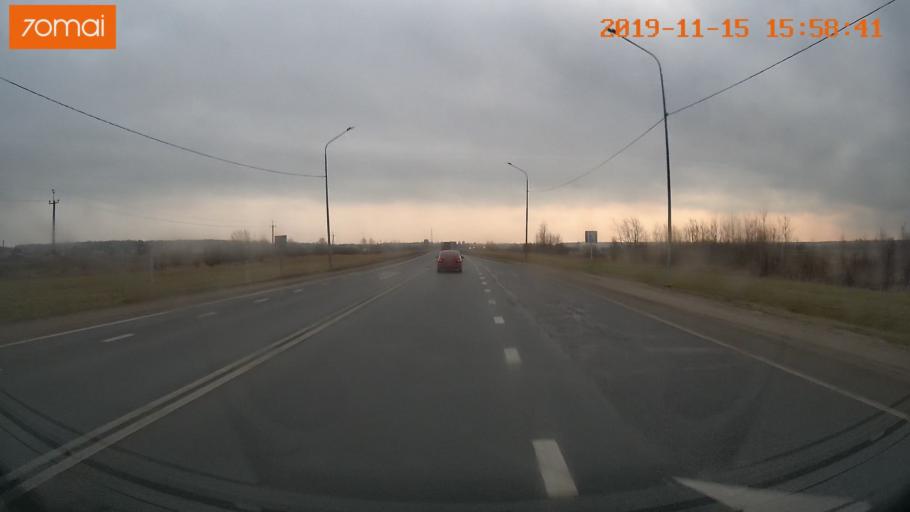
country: RU
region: Jaroslavl
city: Yaroslavl
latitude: 57.8167
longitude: 39.9531
